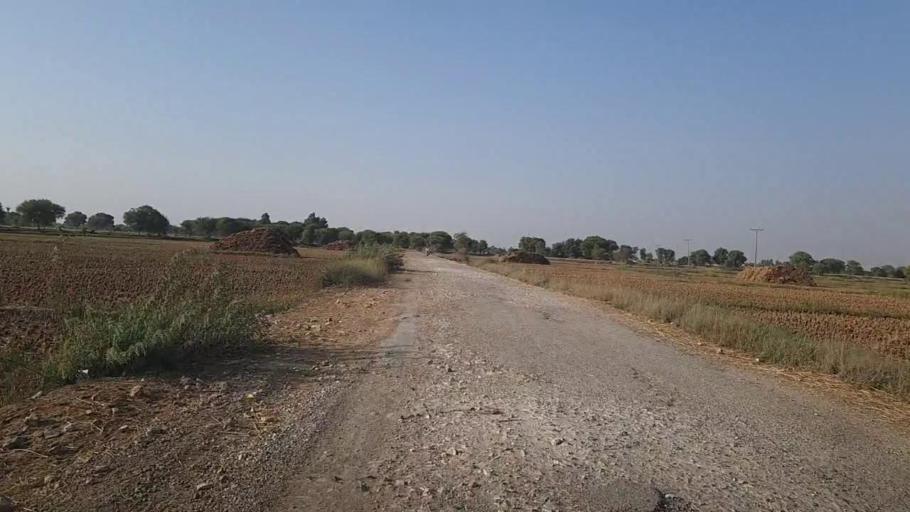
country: PK
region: Sindh
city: Kashmor
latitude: 28.4200
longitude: 69.4089
